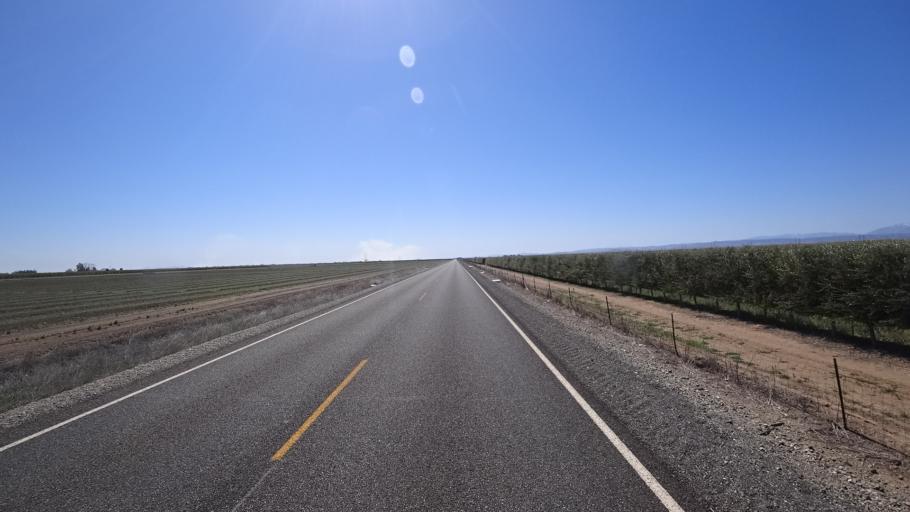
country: US
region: California
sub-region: Glenn County
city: Willows
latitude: 39.5945
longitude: -122.2498
